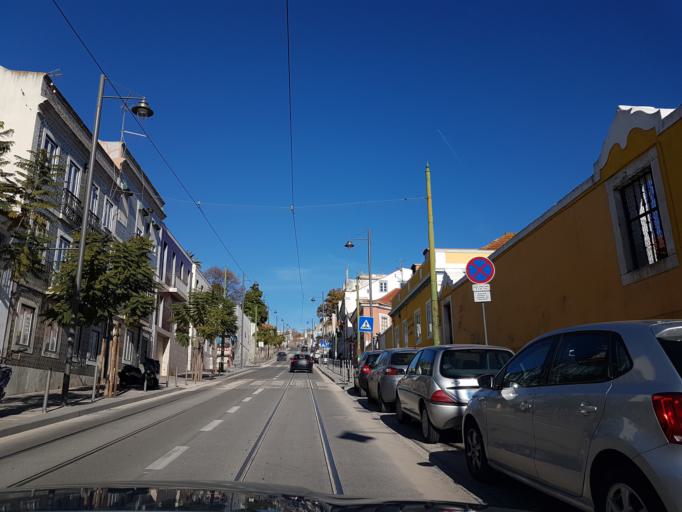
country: PT
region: Lisbon
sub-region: Oeiras
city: Alges
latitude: 38.7052
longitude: -9.1993
